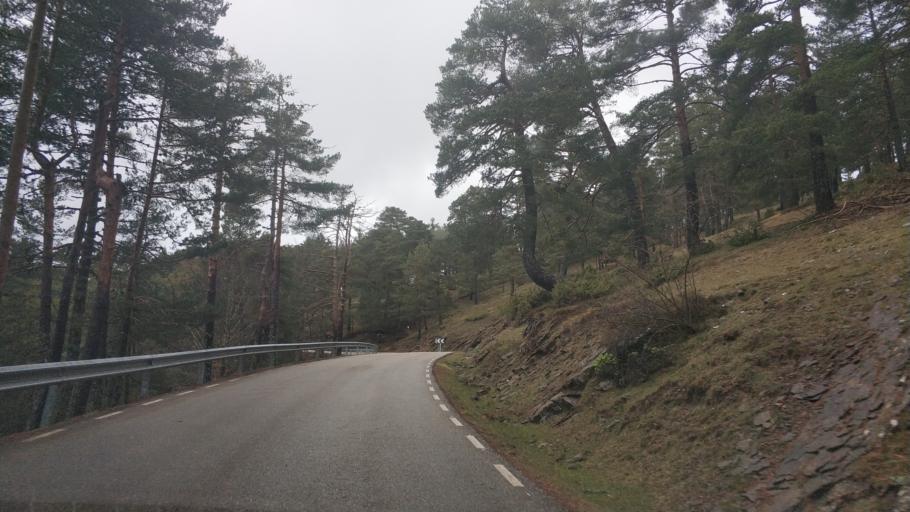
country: ES
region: Castille and Leon
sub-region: Provincia de Burgos
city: Neila
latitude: 42.0410
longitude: -3.0080
